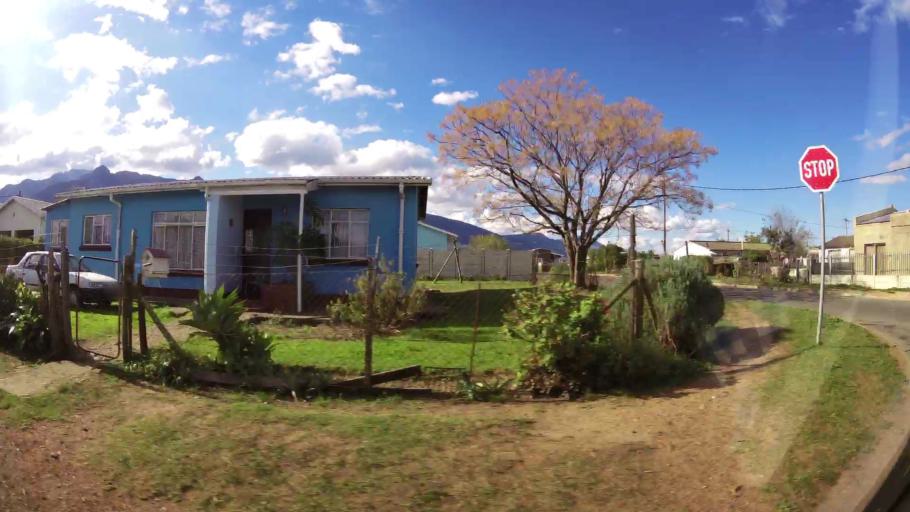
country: ZA
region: Western Cape
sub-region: Overberg District Municipality
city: Swellendam
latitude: -34.0341
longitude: 20.4396
